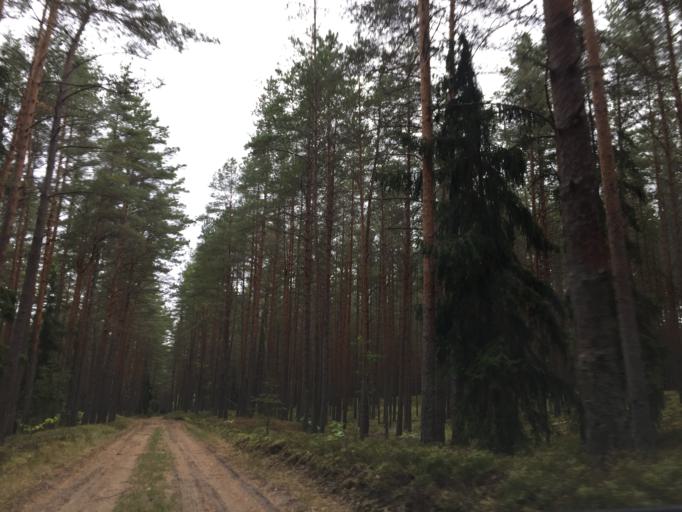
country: LV
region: Salacgrivas
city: Salacgriva
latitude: 57.7083
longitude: 24.3529
